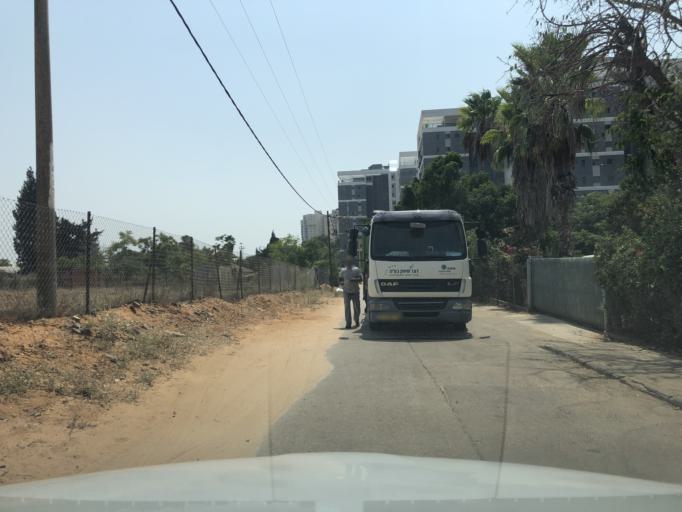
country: IL
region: Central District
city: Ganne Tiqwa
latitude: 32.0666
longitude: 34.8809
